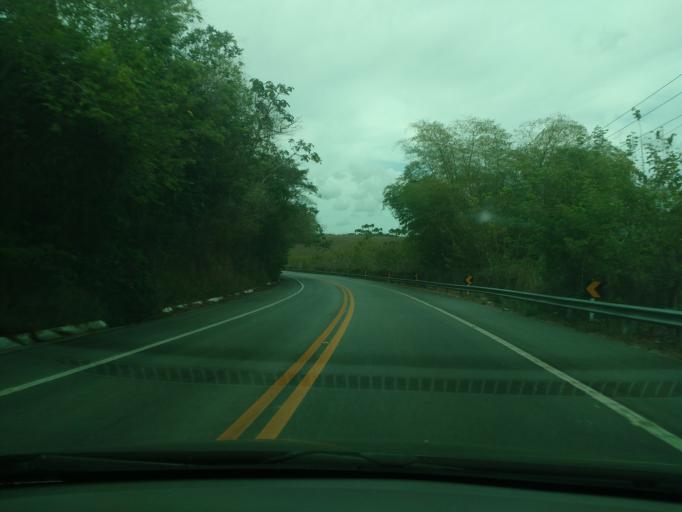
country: BR
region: Alagoas
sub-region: Murici
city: Murici
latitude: -9.2620
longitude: -35.9859
